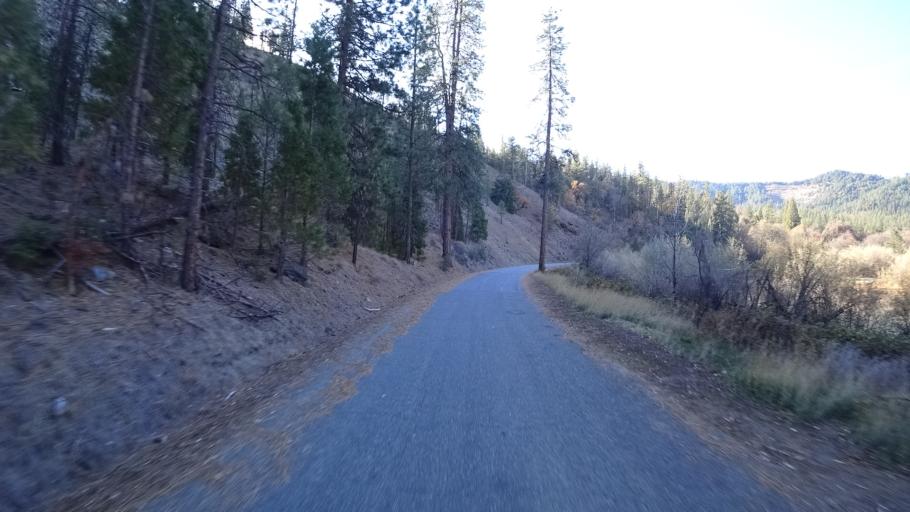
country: US
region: California
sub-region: Siskiyou County
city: Yreka
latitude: 41.8236
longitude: -122.9608
